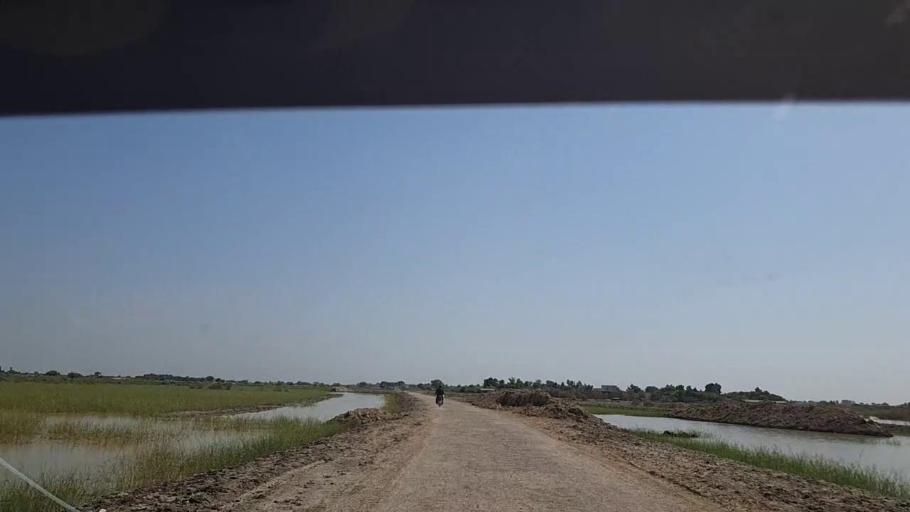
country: PK
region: Sindh
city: Kandhkot
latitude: 28.1745
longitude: 69.1596
